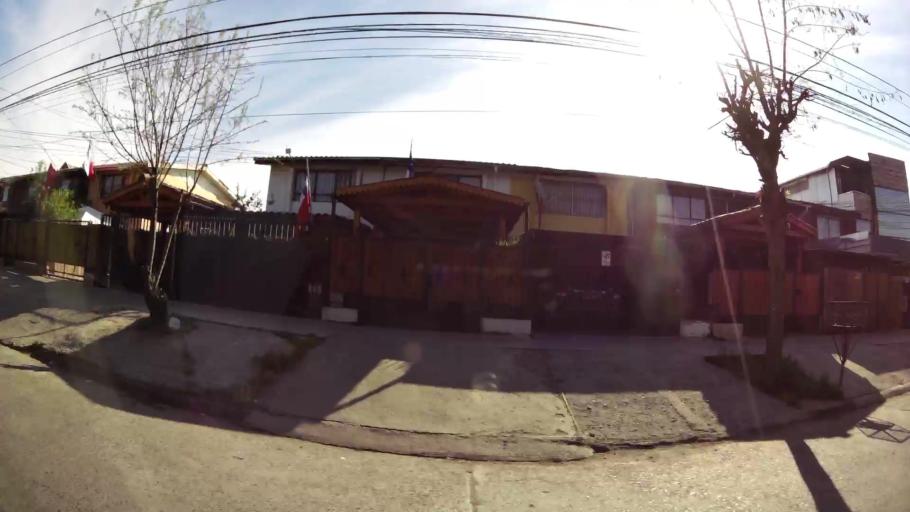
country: CL
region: Santiago Metropolitan
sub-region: Provincia de Cordillera
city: Puente Alto
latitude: -33.6231
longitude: -70.5904
